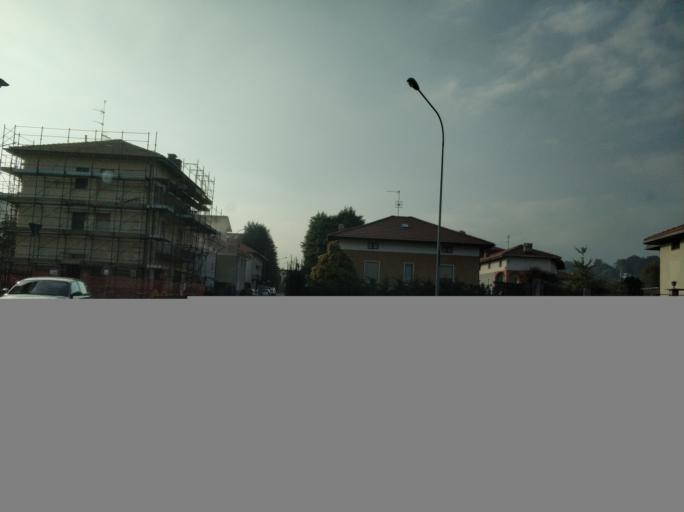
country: IT
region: Piedmont
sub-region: Provincia di Biella
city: Ronco Biellese
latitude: 45.5708
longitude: 8.0783
